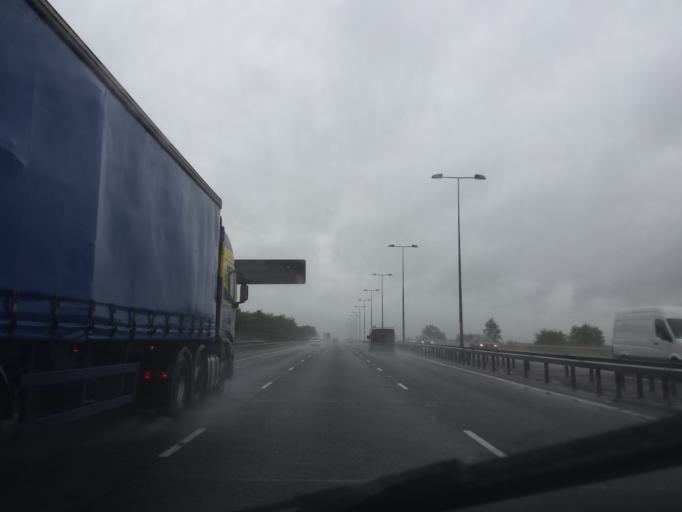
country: GB
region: England
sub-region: Derbyshire
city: Long Eaton
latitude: 52.8903
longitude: -1.3028
